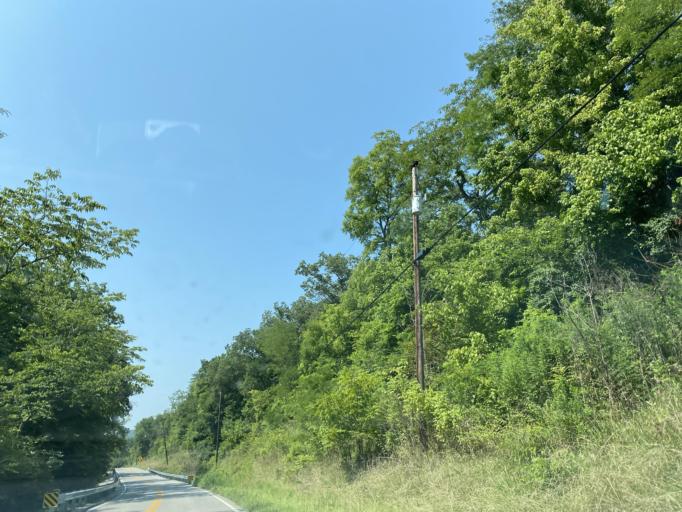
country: US
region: Kentucky
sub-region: Campbell County
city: Claryville
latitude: 38.8925
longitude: -84.4474
